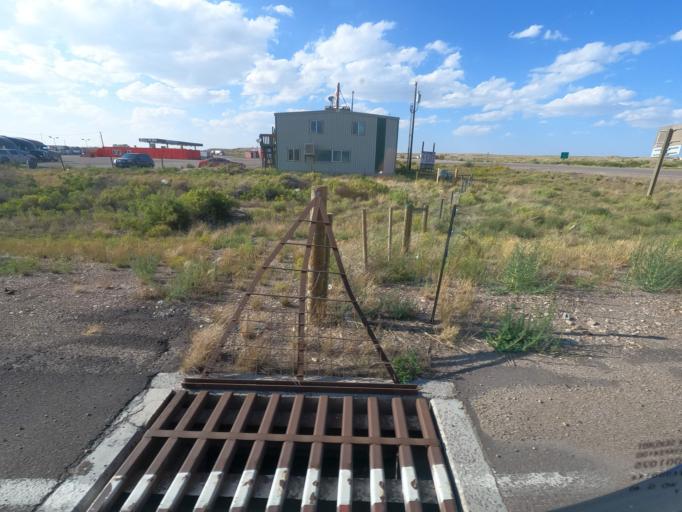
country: US
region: Wyoming
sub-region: Uinta County
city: Lyman
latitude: 41.3676
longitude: -110.3008
